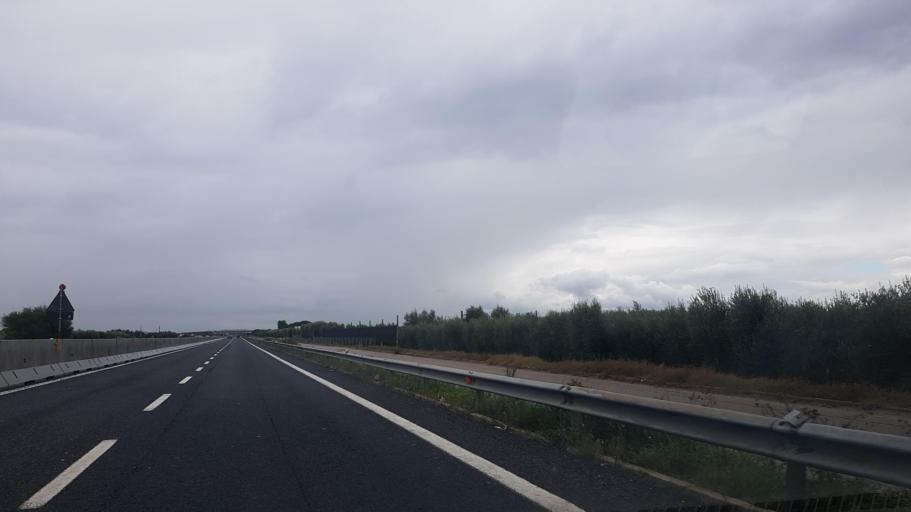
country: IT
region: Apulia
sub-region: Provincia di Taranto
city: Massafra
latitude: 40.5311
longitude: 17.0959
